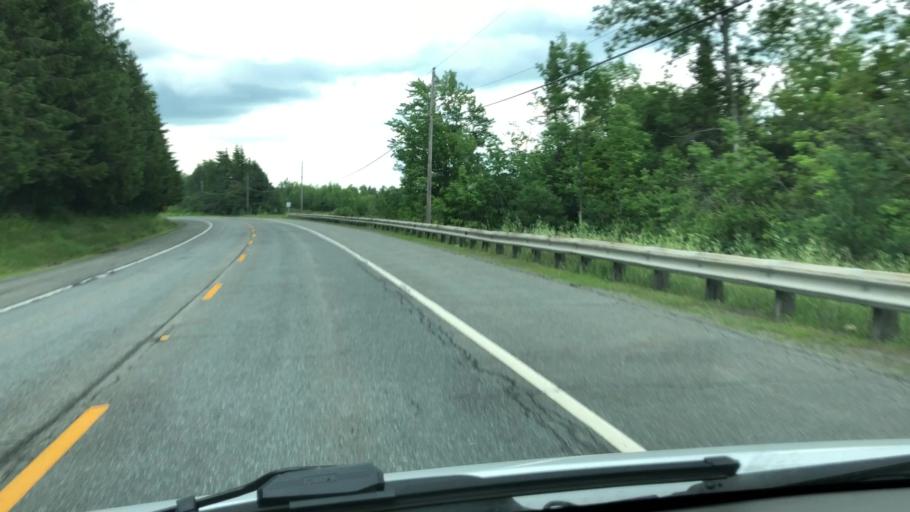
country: US
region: Massachusetts
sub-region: Berkshire County
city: Hinsdale
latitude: 42.5018
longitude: -73.0359
